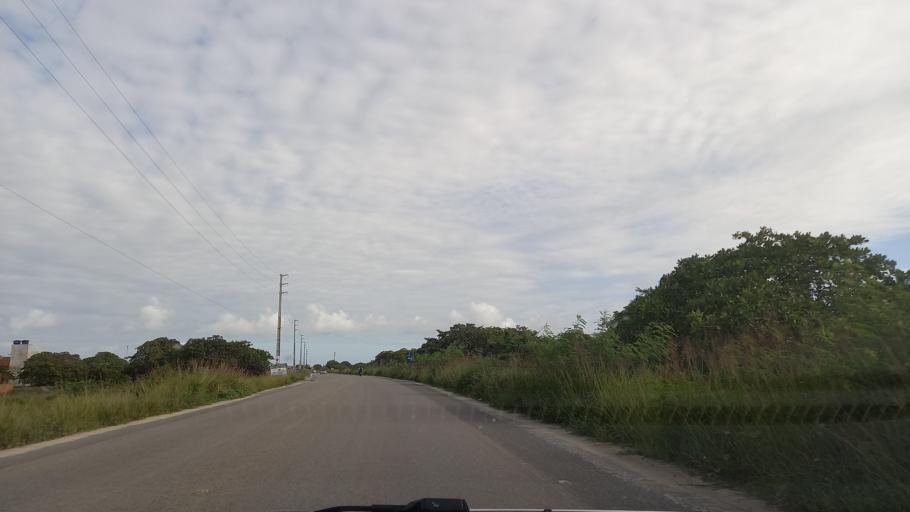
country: BR
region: Pernambuco
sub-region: Tamandare
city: Tamandare
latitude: -8.7353
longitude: -35.0960
